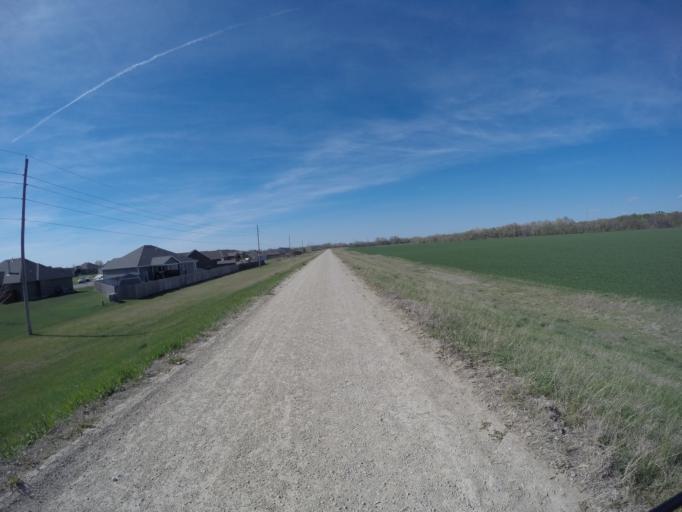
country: US
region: Kansas
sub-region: Saline County
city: Salina
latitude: 38.7995
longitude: -97.5802
